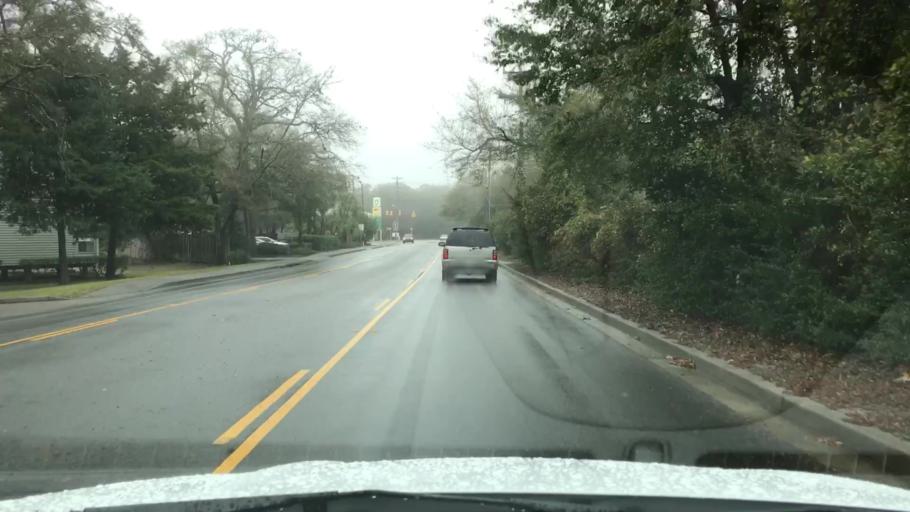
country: US
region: South Carolina
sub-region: Horry County
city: North Myrtle Beach
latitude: 33.7672
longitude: -78.7880
